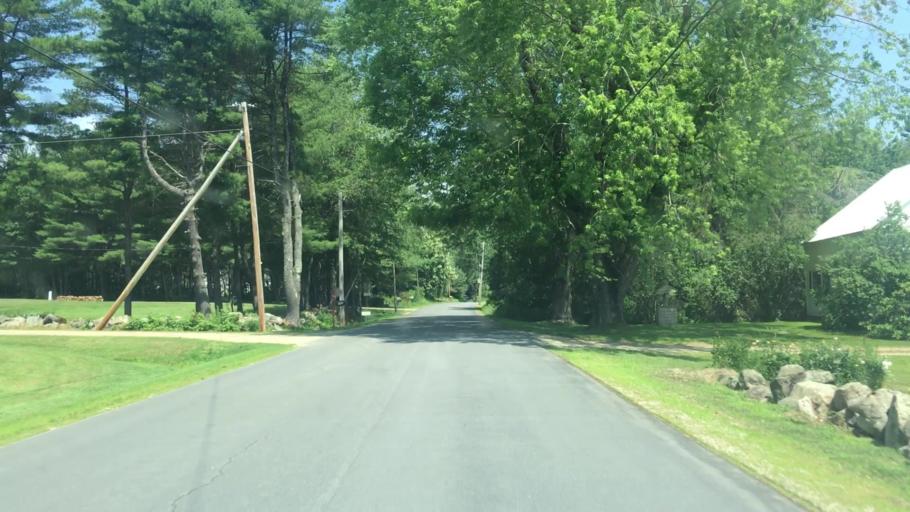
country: US
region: Maine
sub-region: Kennebec County
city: Monmouth
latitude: 44.2692
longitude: -70.0517
